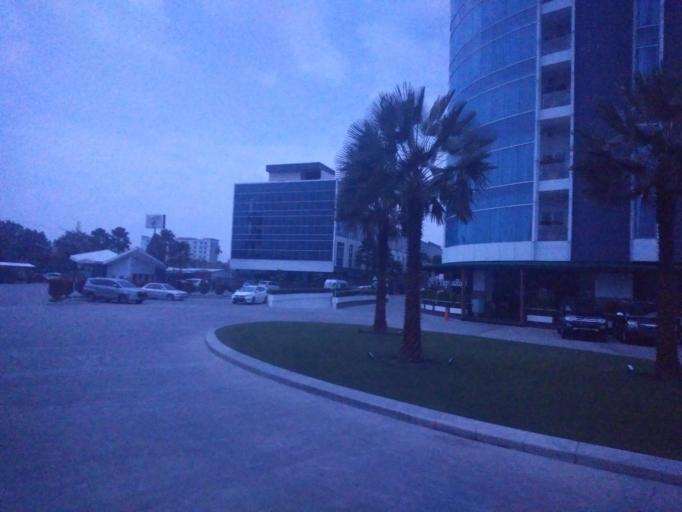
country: ID
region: North Sumatra
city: Percut
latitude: 3.5983
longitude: 98.8301
